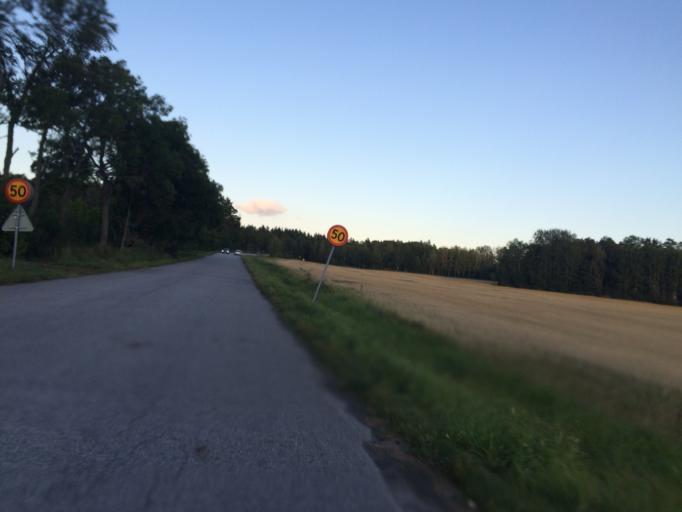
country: SE
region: Soedermanland
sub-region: Eskilstuna Kommun
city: Kvicksund
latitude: 59.4489
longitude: 16.3410
